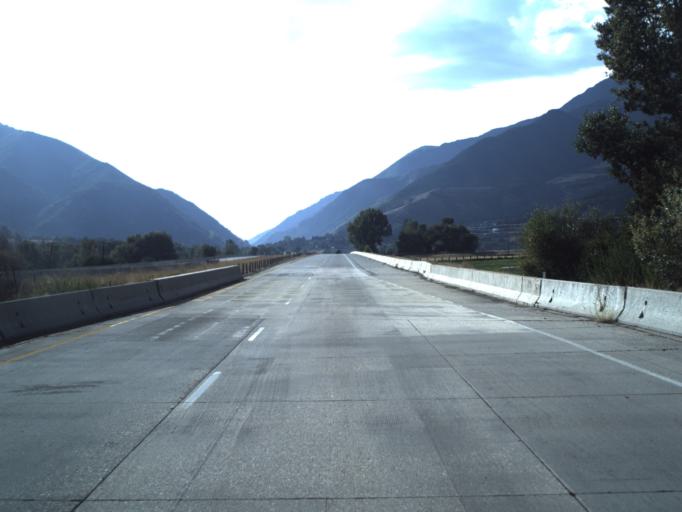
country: US
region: Utah
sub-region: Morgan County
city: Mountain Green
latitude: 41.1381
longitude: -111.8029
